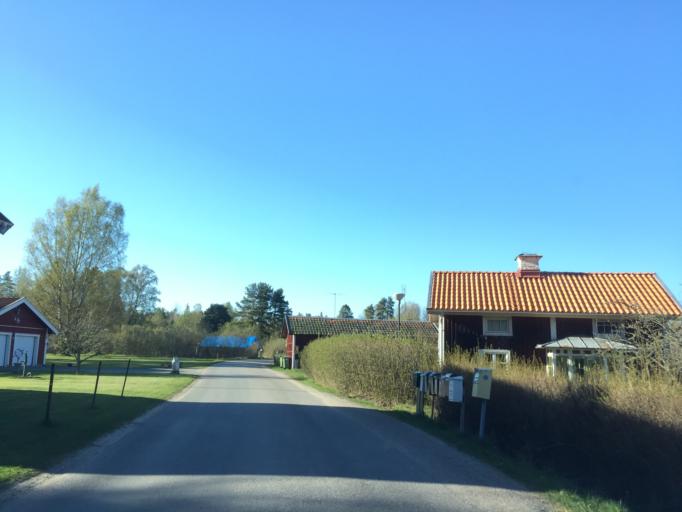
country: SE
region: OErebro
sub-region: Orebro Kommun
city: Odensbacken
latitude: 59.2261
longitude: 15.5635
